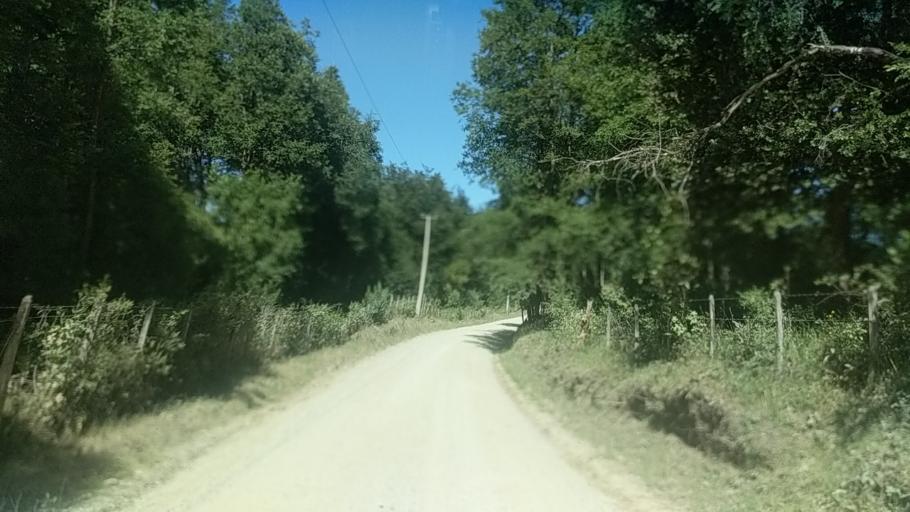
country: CL
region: Araucania
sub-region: Provincia de Cautin
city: Pucon
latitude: -39.0641
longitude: -71.7337
